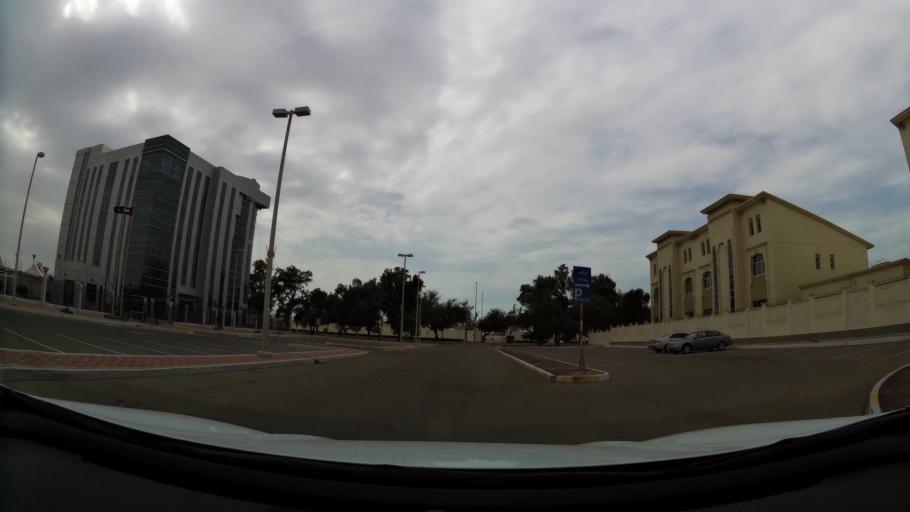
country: AE
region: Abu Dhabi
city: Abu Dhabi
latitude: 24.4334
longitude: 54.4219
